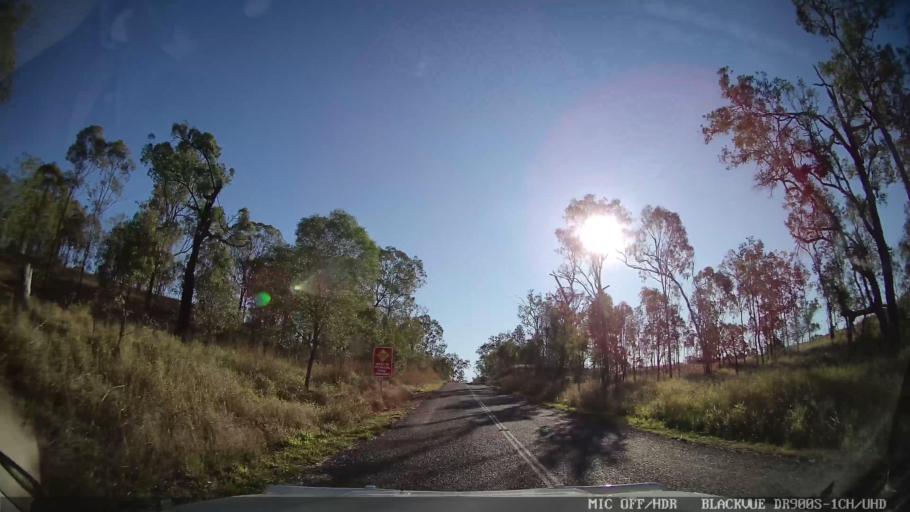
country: AU
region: Queensland
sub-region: Bundaberg
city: Sharon
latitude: -24.8037
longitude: 151.6502
